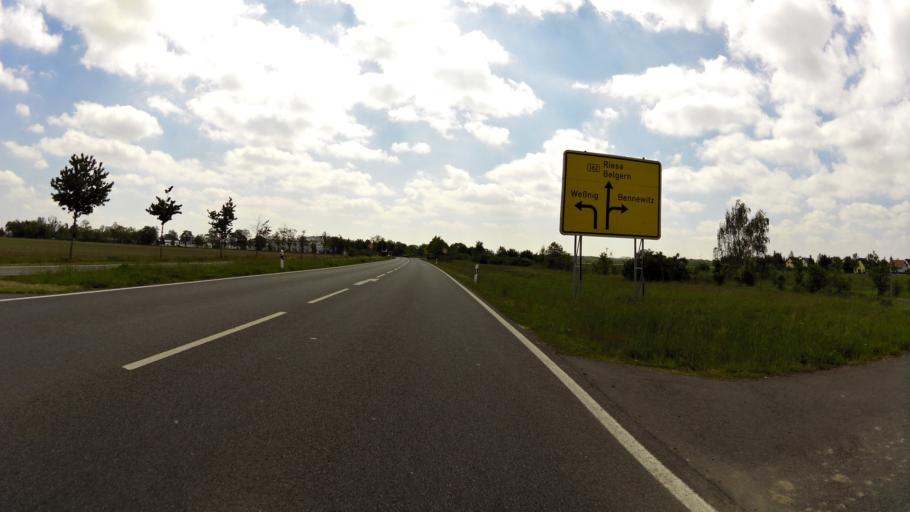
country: DE
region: Saxony
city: Beilrode
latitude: 51.5172
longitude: 13.0358
